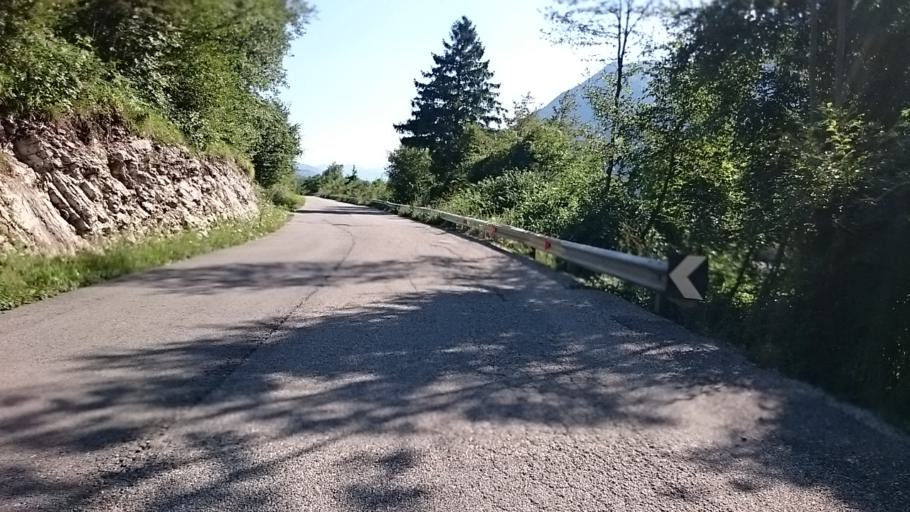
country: IT
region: Veneto
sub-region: Provincia di Belluno
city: Soverzene
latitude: 46.2300
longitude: 12.3024
